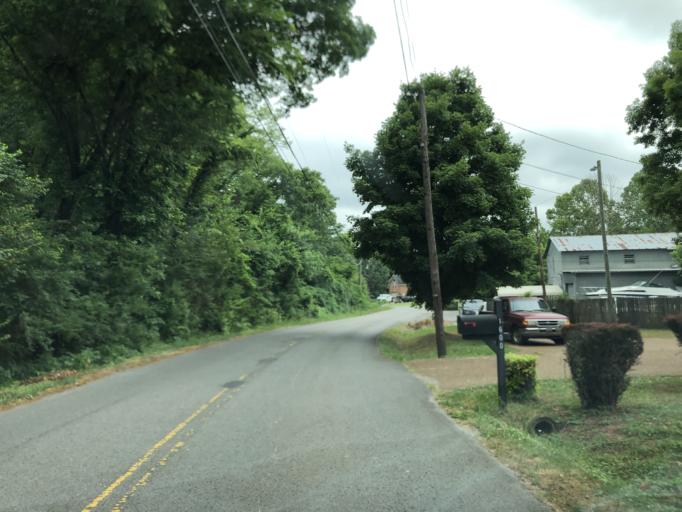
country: US
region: Tennessee
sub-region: Davidson County
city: Goodlettsville
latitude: 36.2880
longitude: -86.7792
